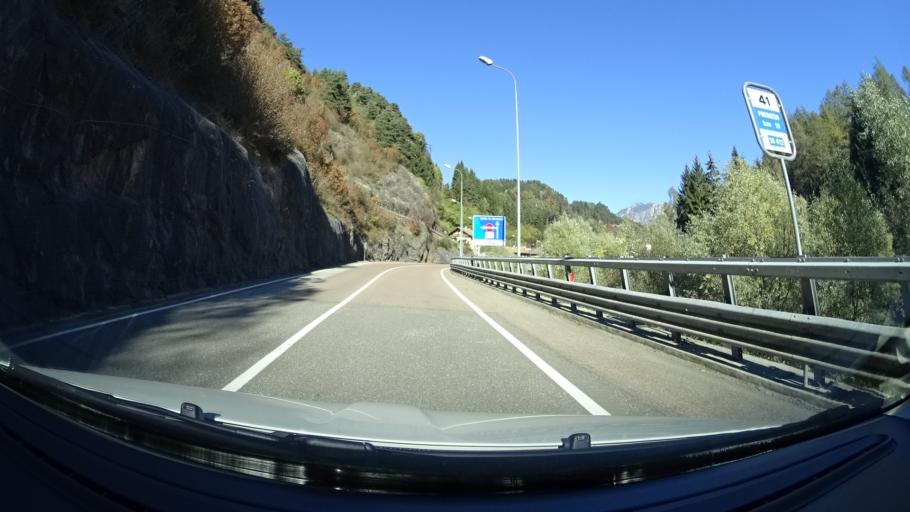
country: IT
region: Trentino-Alto Adige
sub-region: Provincia di Trento
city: Castello Molina di Fiemme
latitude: 46.2697
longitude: 11.4107
